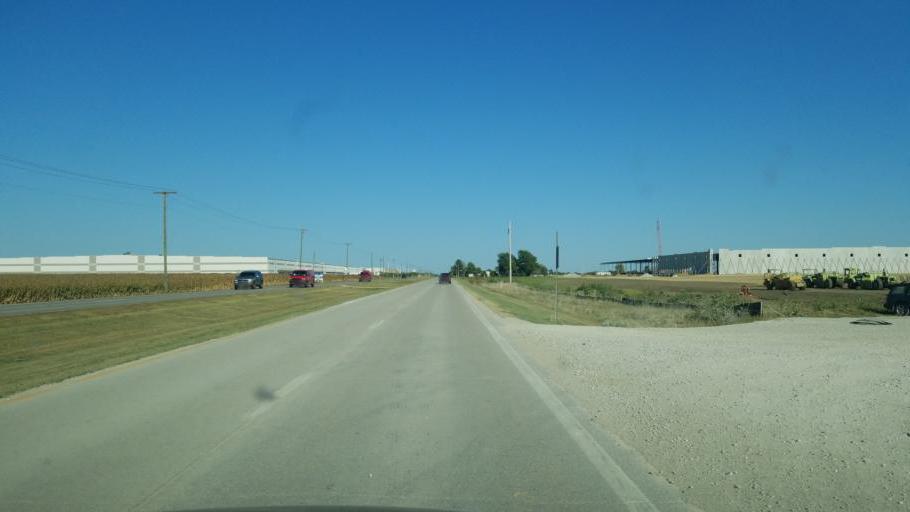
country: US
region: Ohio
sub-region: Madison County
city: West Jefferson
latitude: 39.9411
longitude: -83.3362
